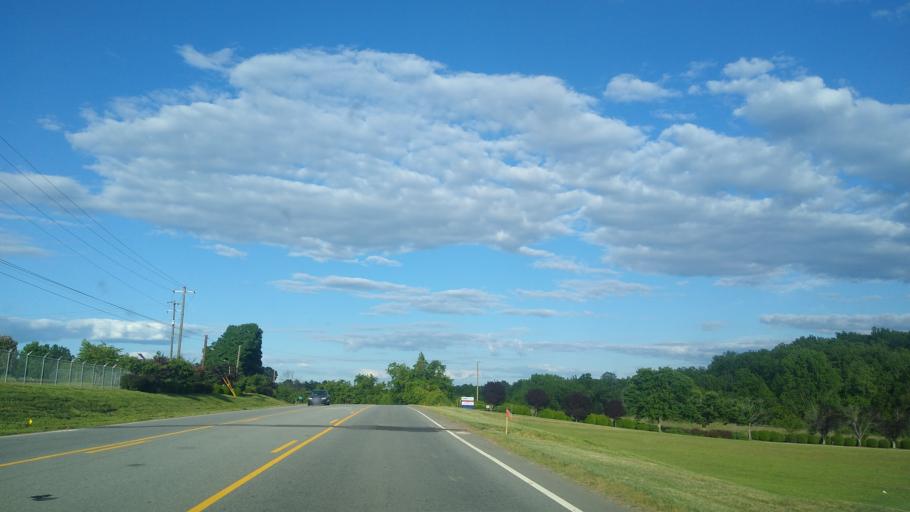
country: US
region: North Carolina
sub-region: Guilford County
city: McLeansville
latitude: 36.1737
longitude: -79.7205
